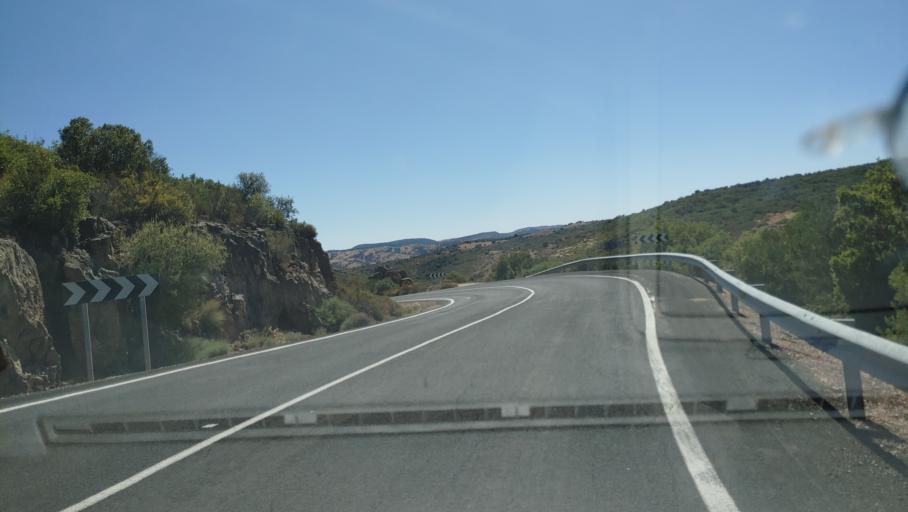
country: ES
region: Castille-La Mancha
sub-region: Provincia de Ciudad Real
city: Albaladejo
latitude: 38.5238
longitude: -2.7830
